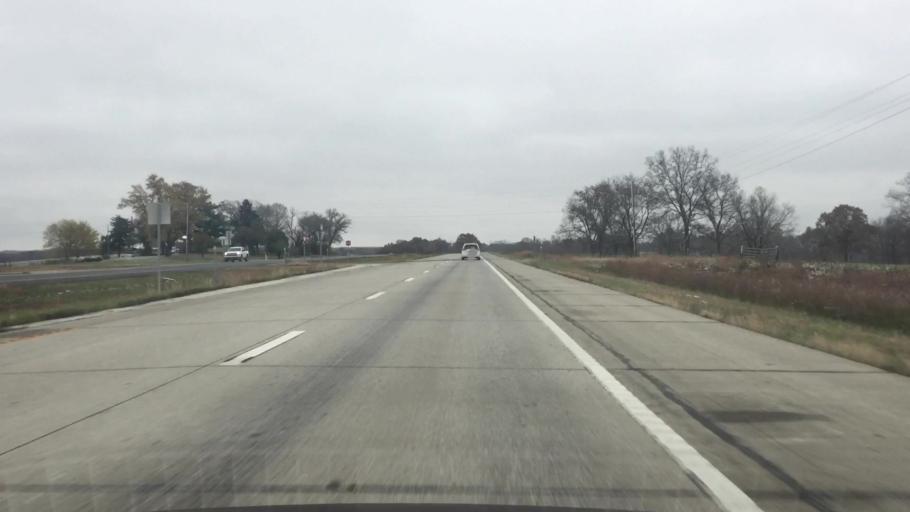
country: US
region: Missouri
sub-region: Saint Clair County
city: Osceola
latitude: 38.0281
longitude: -93.6750
